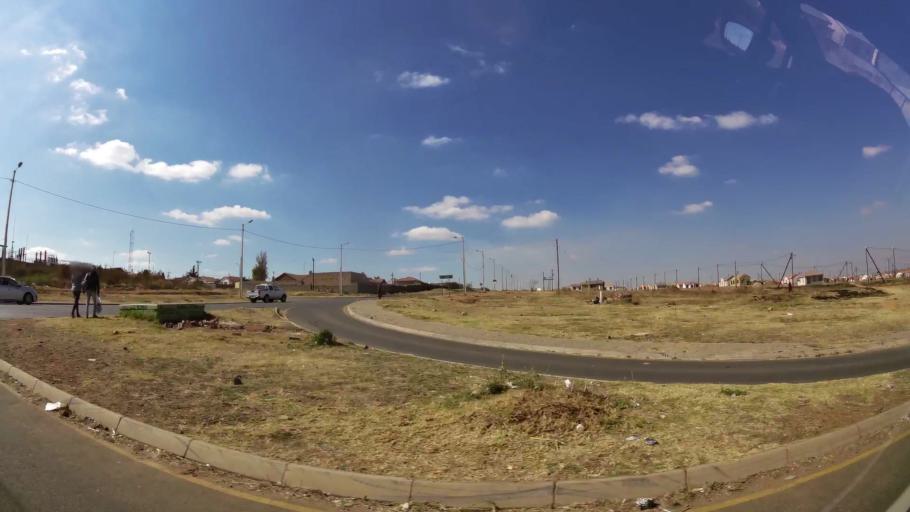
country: ZA
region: Gauteng
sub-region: West Rand District Municipality
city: Randfontein
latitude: -26.1659
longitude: 27.7704
